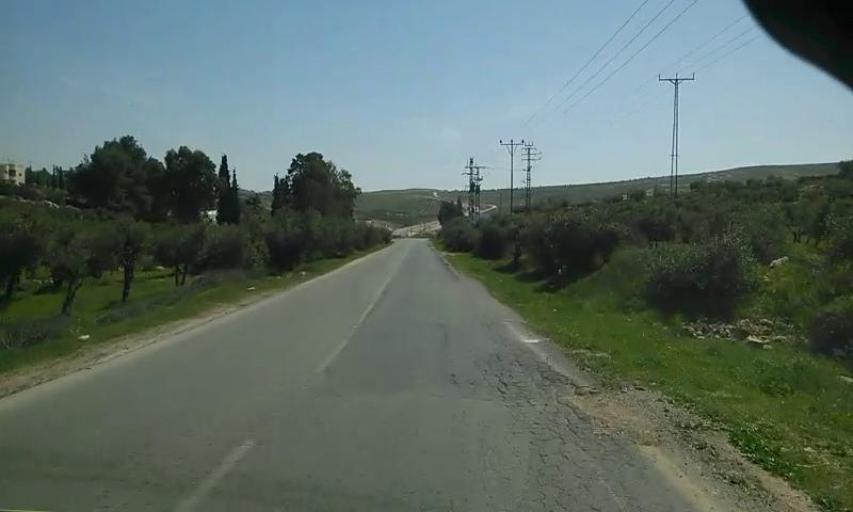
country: PS
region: West Bank
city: Marah Rabbah
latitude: 31.6297
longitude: 35.2051
